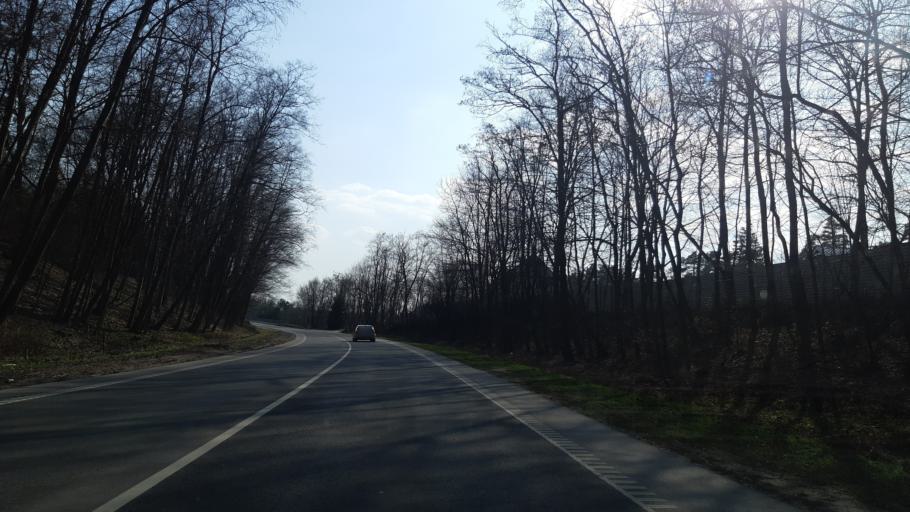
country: LT
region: Kauno apskritis
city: Dainava (Kaunas)
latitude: 54.8693
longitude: 23.9879
